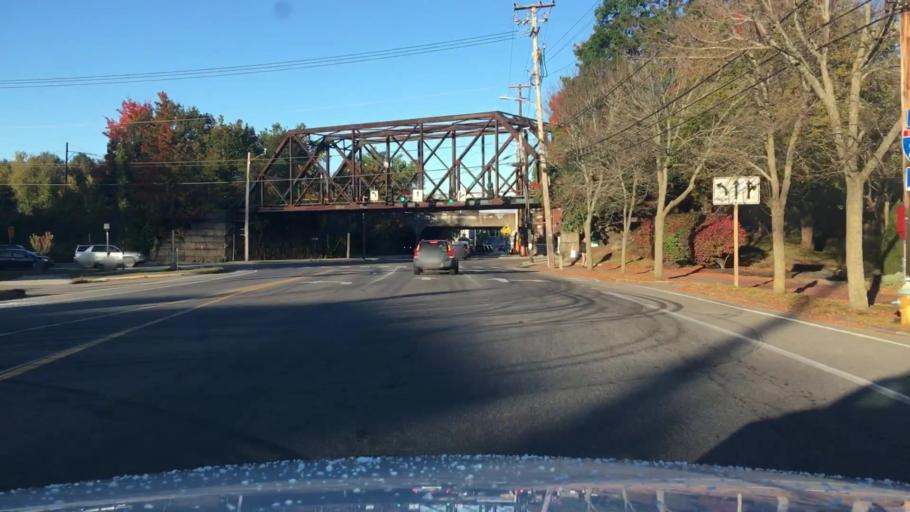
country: US
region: Maine
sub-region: Cumberland County
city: Portland
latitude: 43.6559
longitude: -70.2794
